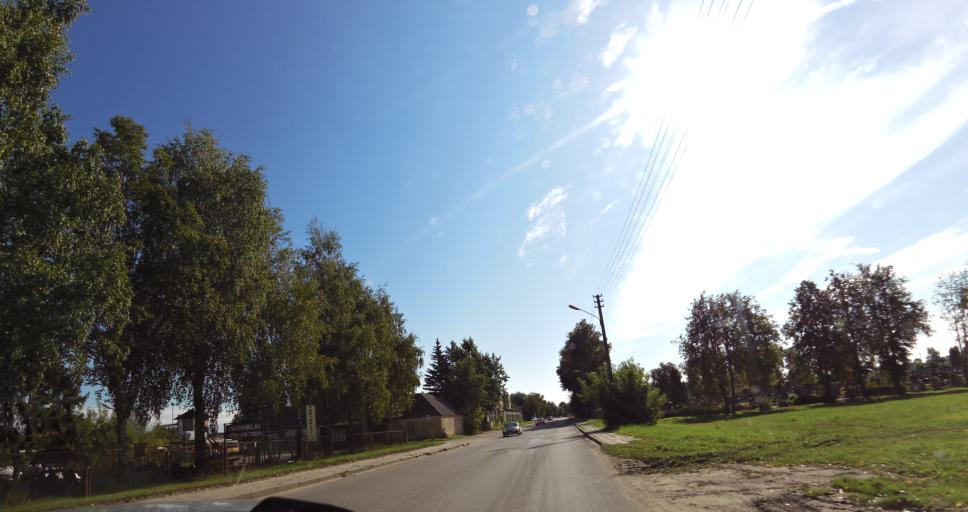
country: LT
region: Panevezys
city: Pasvalys
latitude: 56.0658
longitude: 24.3889
